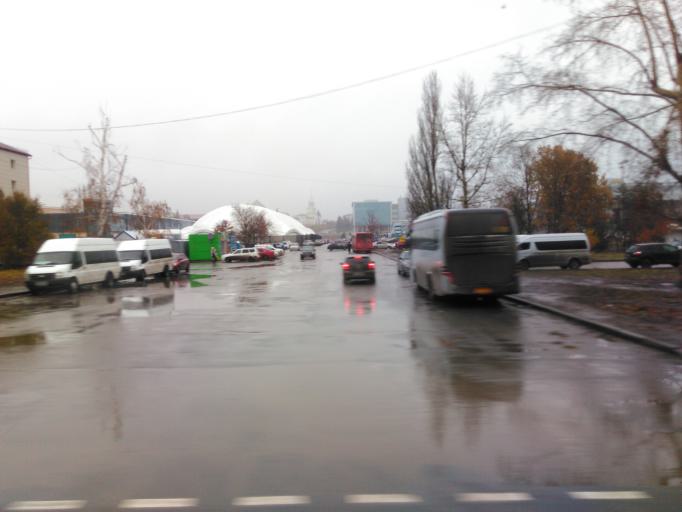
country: RU
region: Tatarstan
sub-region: Gorod Kazan'
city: Kazan
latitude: 55.7922
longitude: 49.0983
